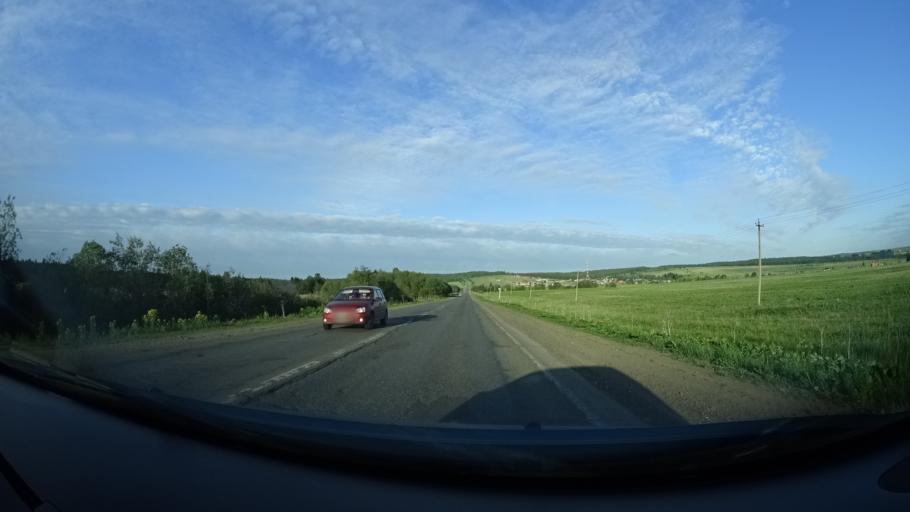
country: RU
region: Perm
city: Kultayevo
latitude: 57.8581
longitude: 55.8642
